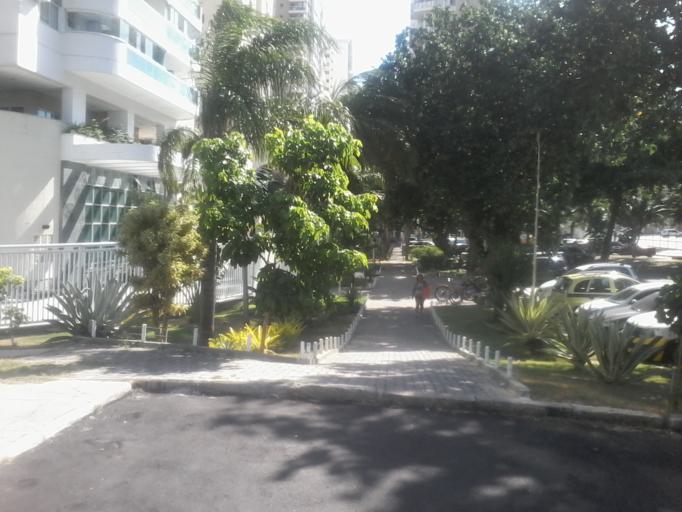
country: BR
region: Rio de Janeiro
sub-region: Nilopolis
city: Nilopolis
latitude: -23.0215
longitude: -43.4861
